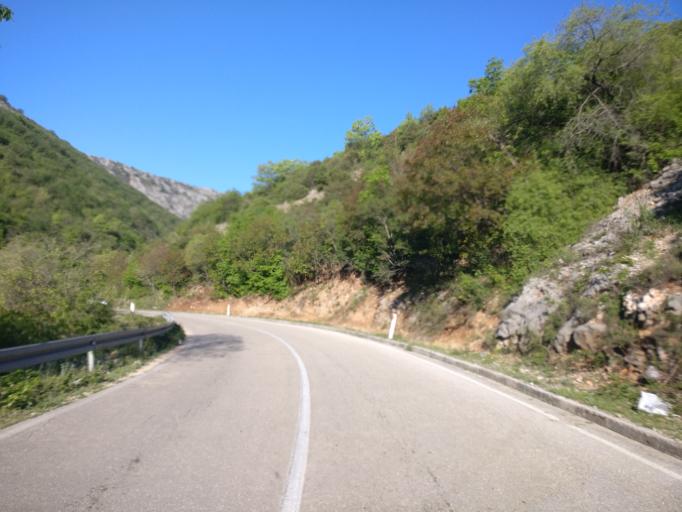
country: BA
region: Federation of Bosnia and Herzegovina
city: Stolac
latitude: 43.0723
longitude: 18.0523
